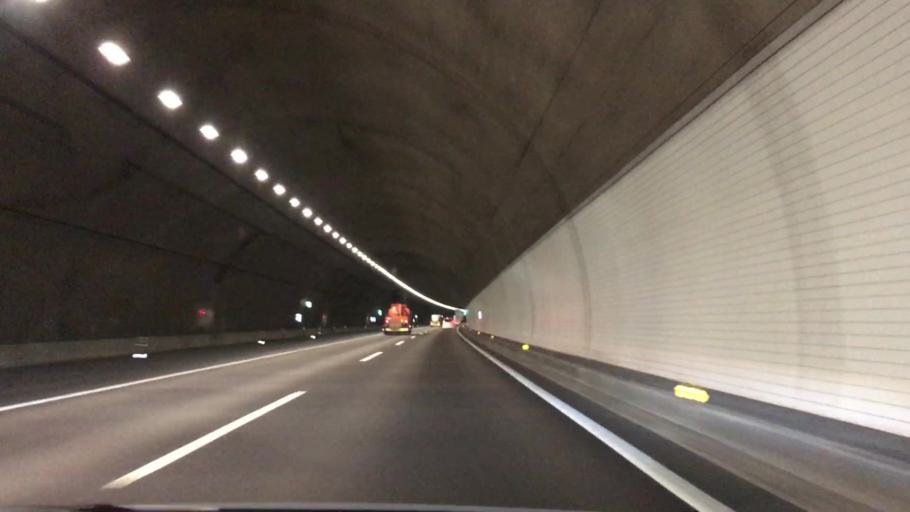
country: JP
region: Shizuoka
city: Hamakita
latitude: 34.8711
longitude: 137.6738
